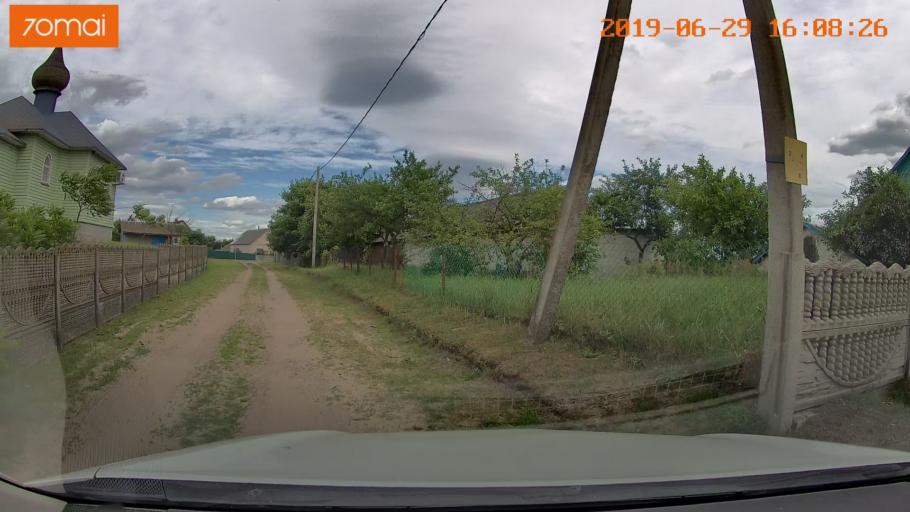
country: BY
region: Brest
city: Luninyets
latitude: 52.2048
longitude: 27.0099
